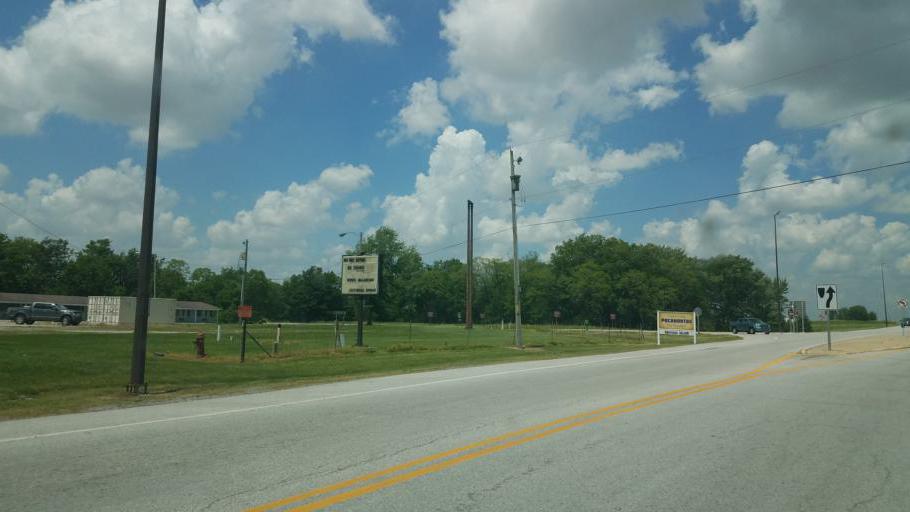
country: US
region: Illinois
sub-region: Bond County
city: Greenville
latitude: 38.8290
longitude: -89.5453
